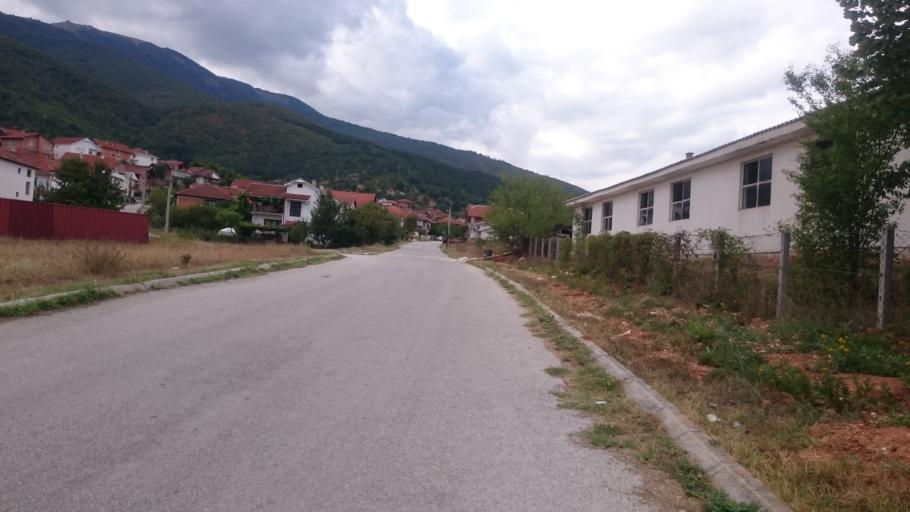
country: MK
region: Makedonski Brod
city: Makedonski Brod
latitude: 41.5166
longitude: 21.2188
